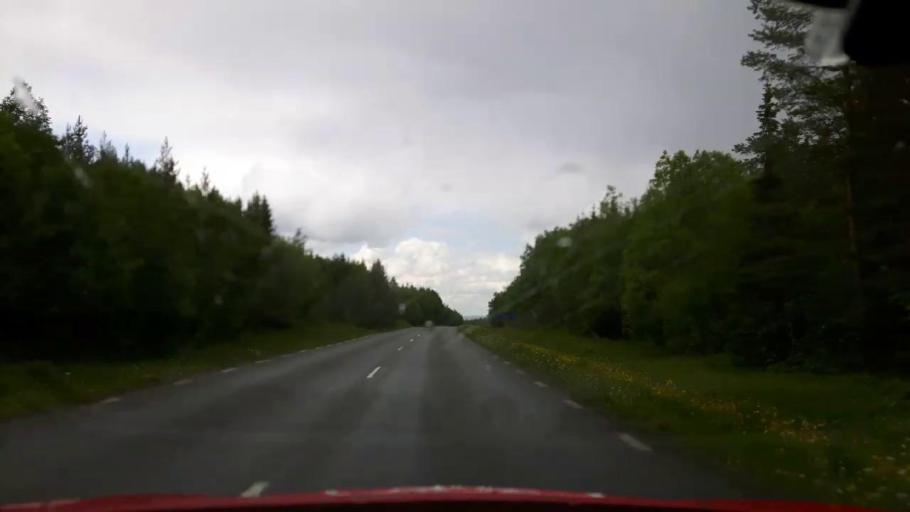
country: SE
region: Jaemtland
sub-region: Krokoms Kommun
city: Krokom
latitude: 63.4625
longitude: 14.1918
